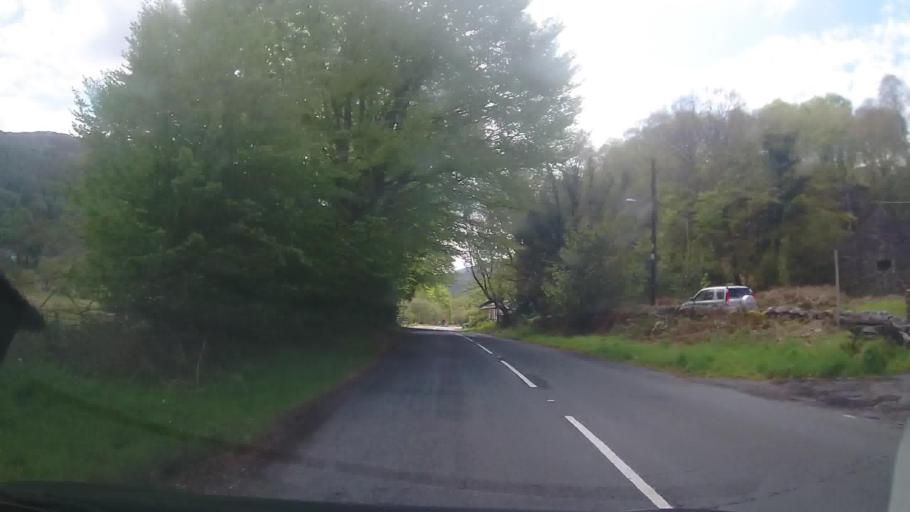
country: GB
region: Wales
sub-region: Gwynedd
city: Penrhyndeudraeth
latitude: 53.0173
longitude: -4.0967
